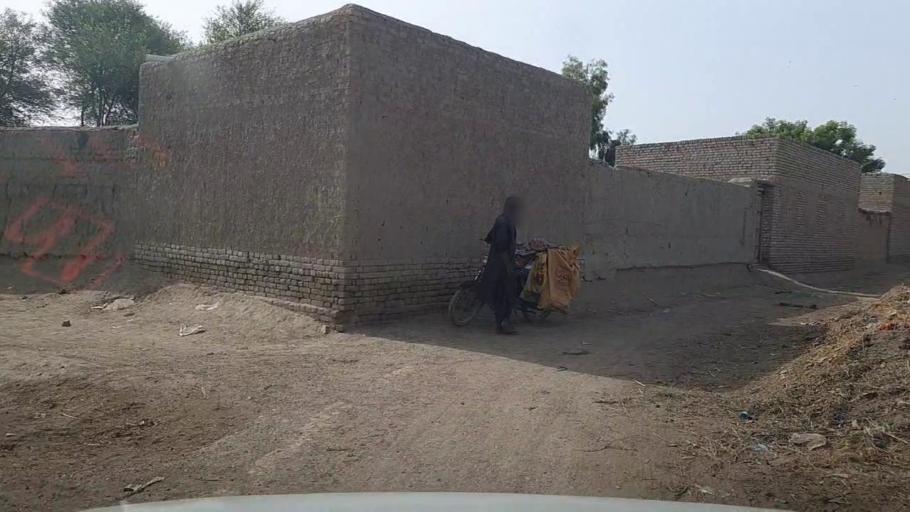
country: PK
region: Sindh
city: Sita Road
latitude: 27.0987
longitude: 67.8251
